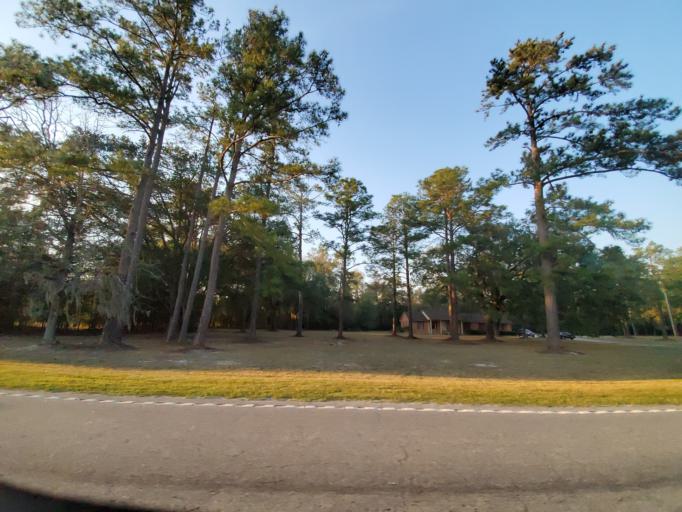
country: US
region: South Carolina
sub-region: Dorchester County
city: Saint George
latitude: 33.0482
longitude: -80.5246
